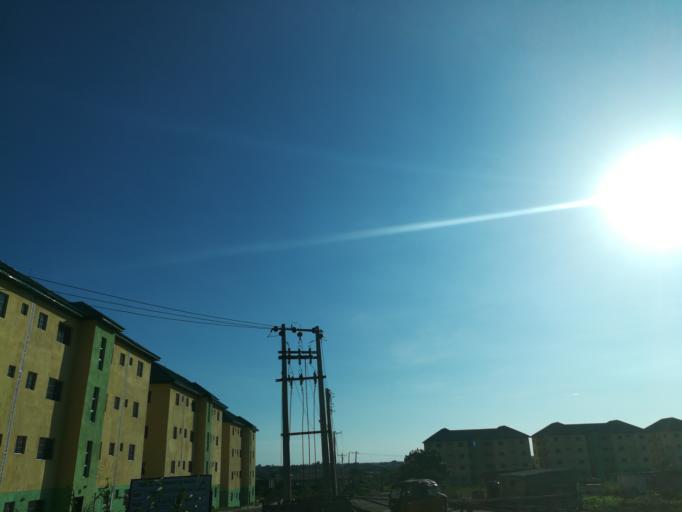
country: NG
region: Lagos
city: Ikorodu
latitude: 6.5610
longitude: 3.5363
